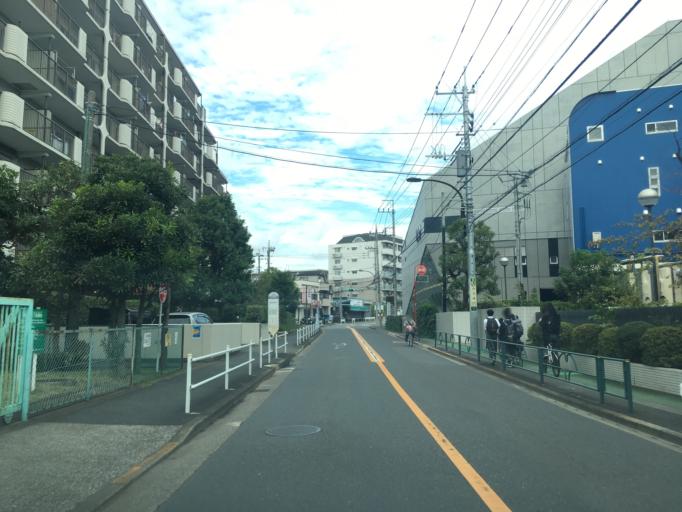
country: JP
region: Tokyo
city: Chofugaoka
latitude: 35.6444
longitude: 139.5390
